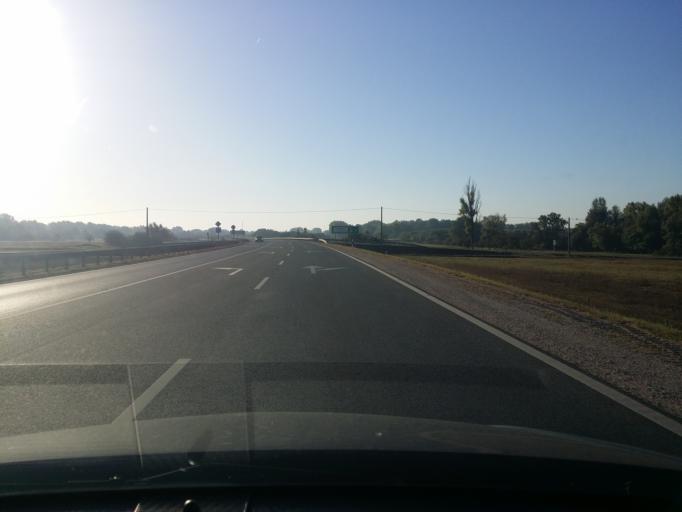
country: HU
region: Bacs-Kiskun
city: Kecskemet
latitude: 46.9194
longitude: 19.7262
